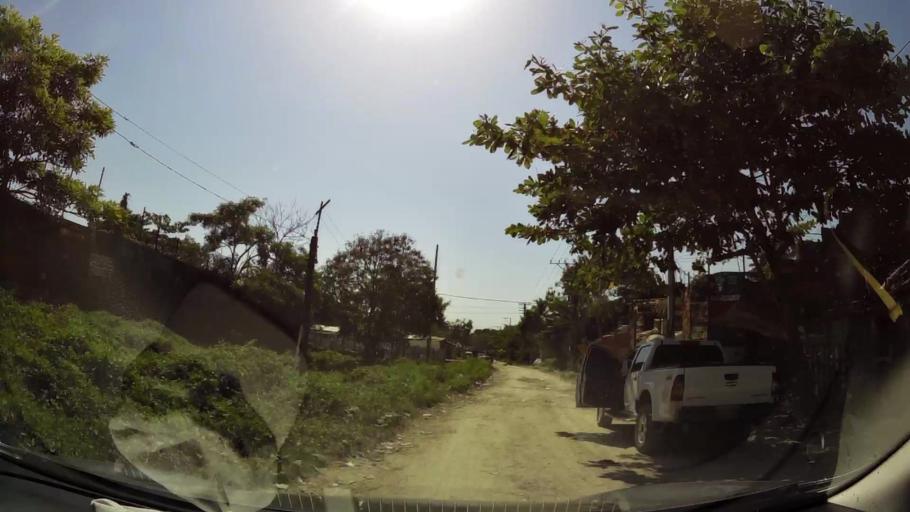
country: CO
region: Bolivar
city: Cartagena
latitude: 10.3696
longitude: -75.4938
